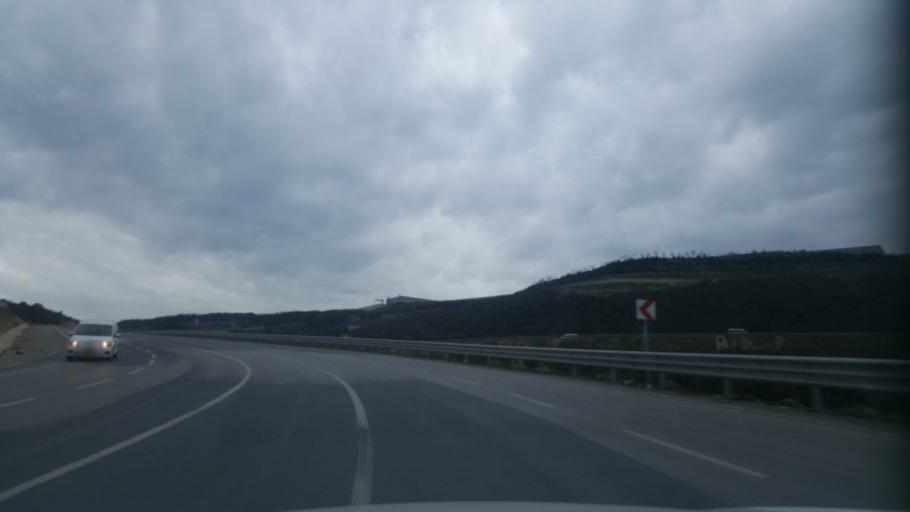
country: TR
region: Kocaeli
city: Tavsanli
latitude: 40.8410
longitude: 29.5498
